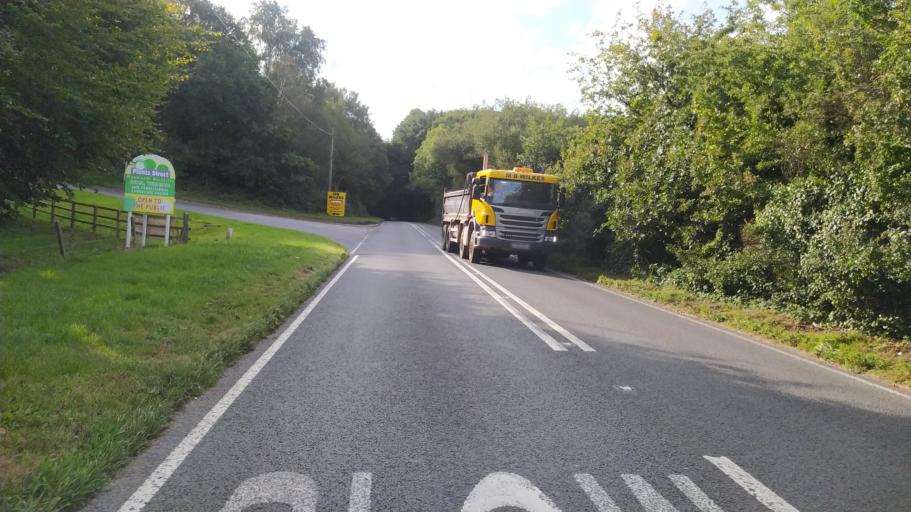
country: GB
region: England
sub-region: Dorset
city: Lytchett Matravers
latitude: 50.7709
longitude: -2.0666
